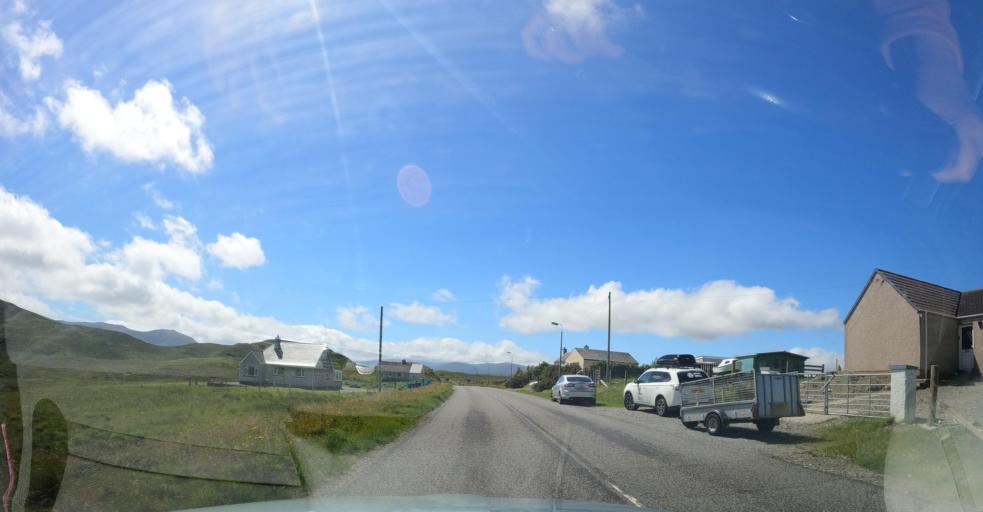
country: GB
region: Scotland
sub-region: Eilean Siar
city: Harris
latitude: 58.0852
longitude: -6.6398
